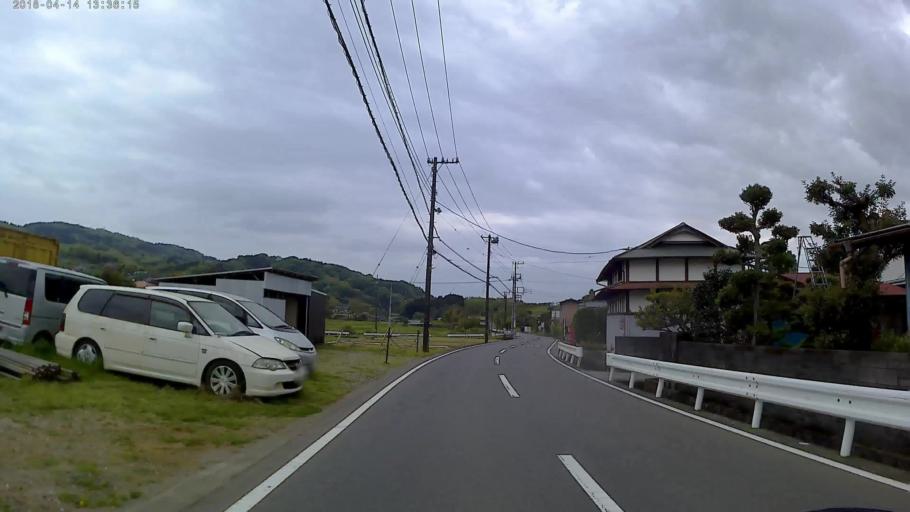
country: JP
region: Kanagawa
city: Hadano
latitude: 35.3309
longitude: 139.1642
